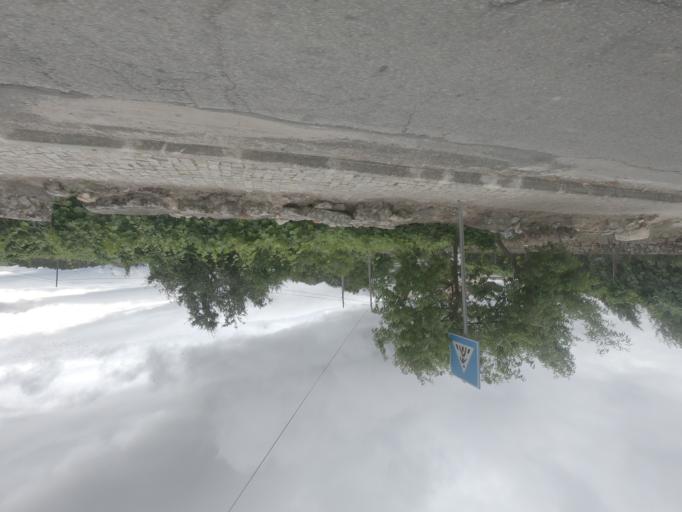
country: PT
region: Vila Real
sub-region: Sabrosa
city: Sabrosa
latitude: 41.2699
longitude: -7.5041
